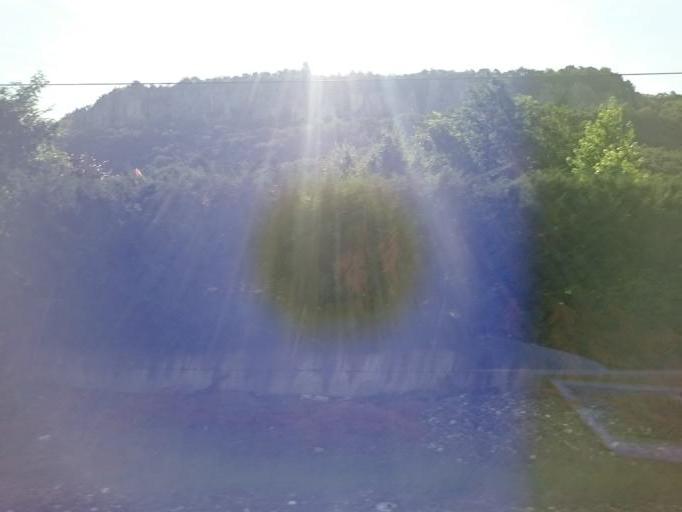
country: IT
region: Veneto
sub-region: Provincia di Verona
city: Volargne
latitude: 45.5403
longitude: 10.8232
